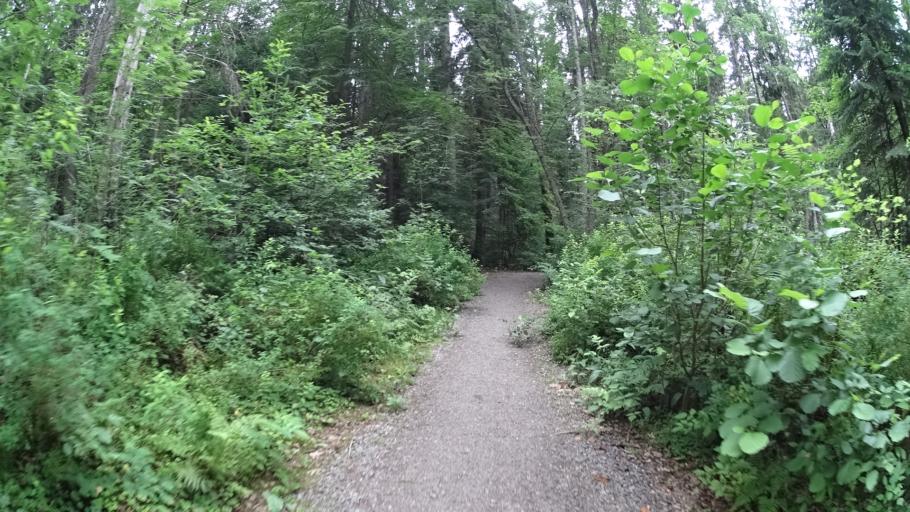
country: FI
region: Uusimaa
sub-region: Helsinki
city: Kauniainen
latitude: 60.2344
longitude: 24.7079
